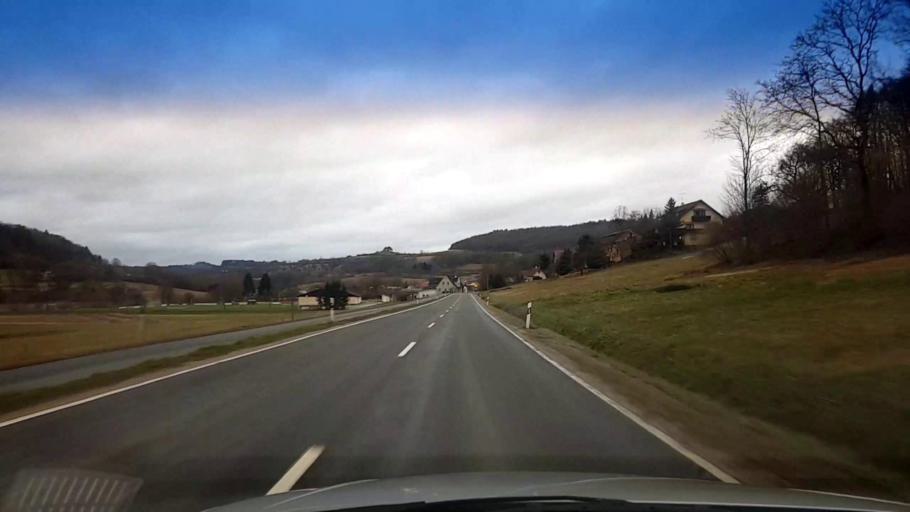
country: DE
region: Bavaria
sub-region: Upper Franconia
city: Wattendorf
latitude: 50.0575
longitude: 11.0748
